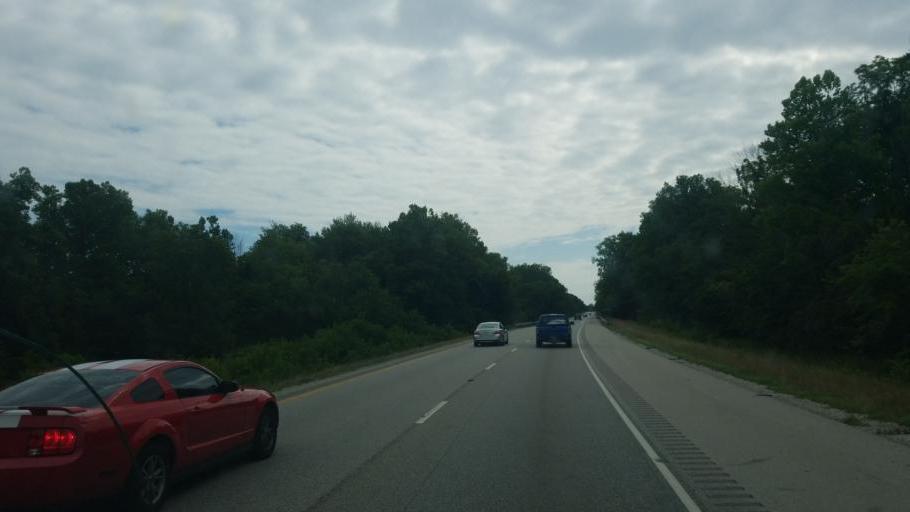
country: US
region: Indiana
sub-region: Vigo County
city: Seelyville
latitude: 39.4425
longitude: -87.2714
